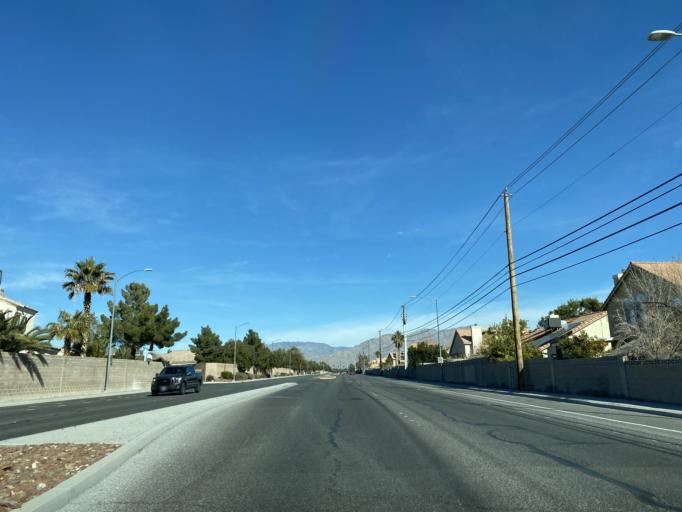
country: US
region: Nevada
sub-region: Clark County
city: Las Vegas
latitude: 36.2568
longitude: -115.2254
